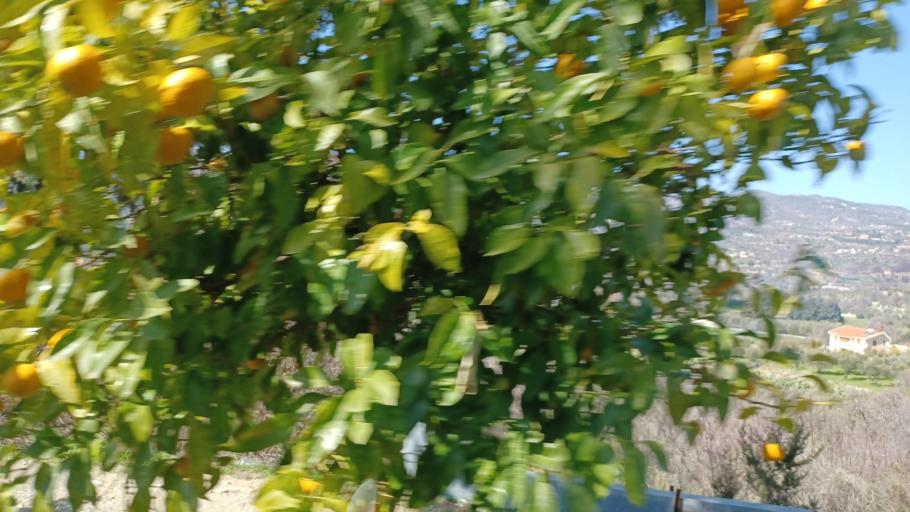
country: CY
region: Limassol
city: Pelendri
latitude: 34.8163
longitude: 32.9154
